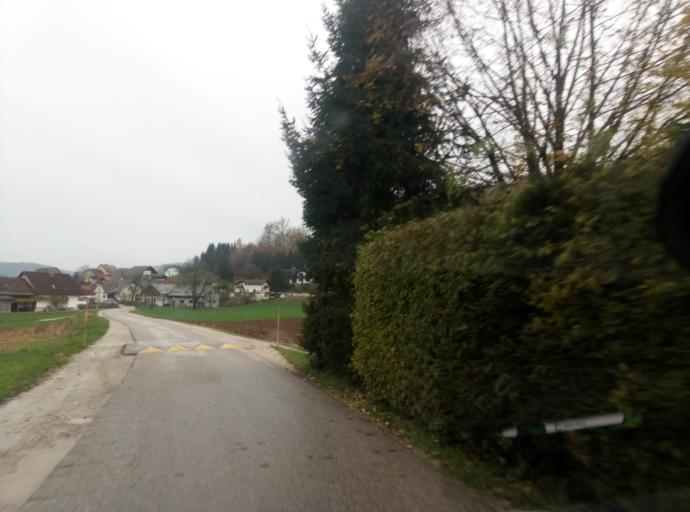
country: SI
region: Vodice
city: Vodice
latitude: 46.1791
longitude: 14.4804
